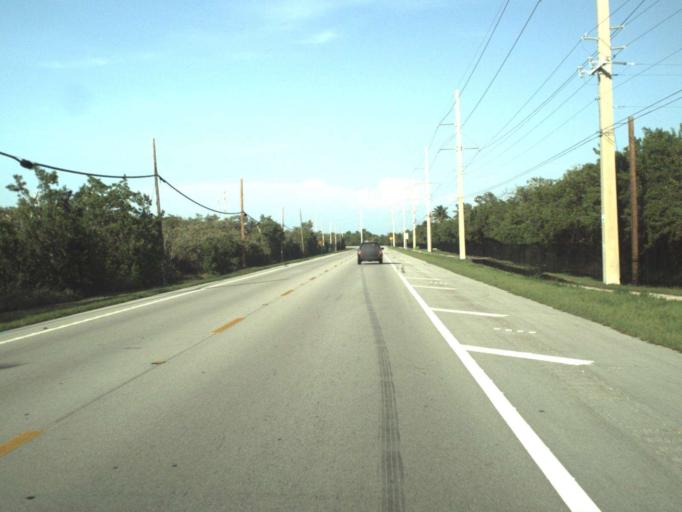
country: US
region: Florida
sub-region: Monroe County
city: Islamorada
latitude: 24.8091
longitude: -80.8337
